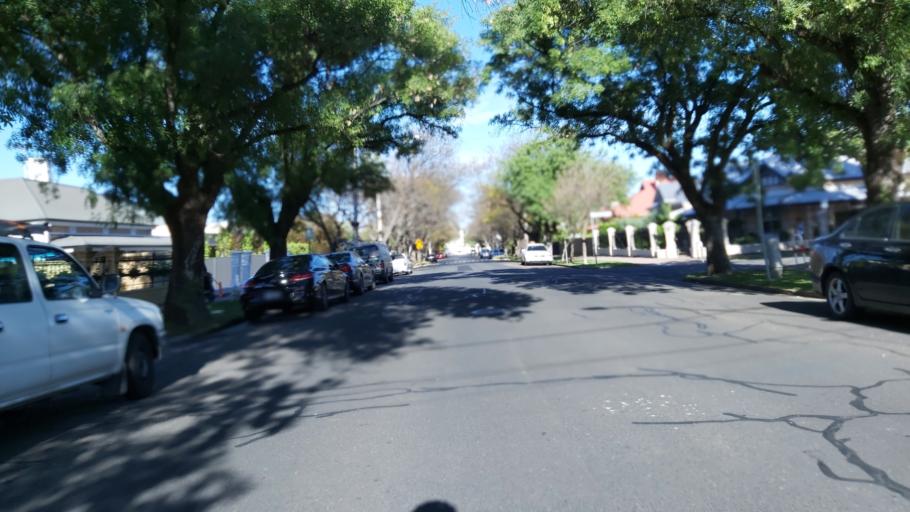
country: AU
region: South Australia
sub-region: Unley
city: Unley
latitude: -34.9467
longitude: 138.6019
